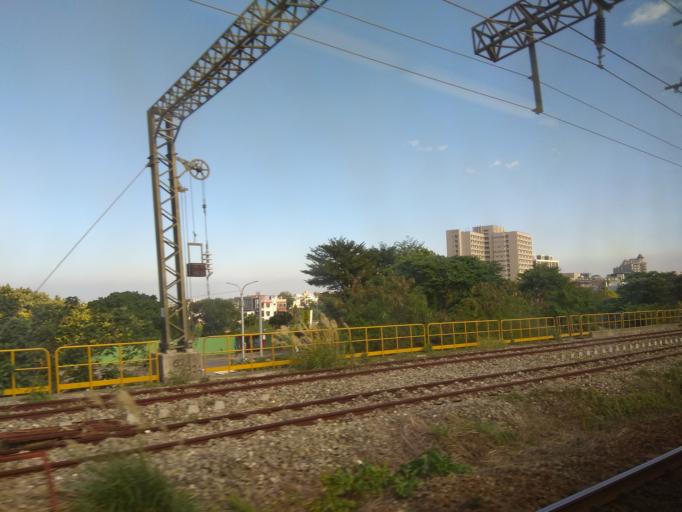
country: TW
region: Taiwan
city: Taoyuan City
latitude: 24.9744
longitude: 121.2647
